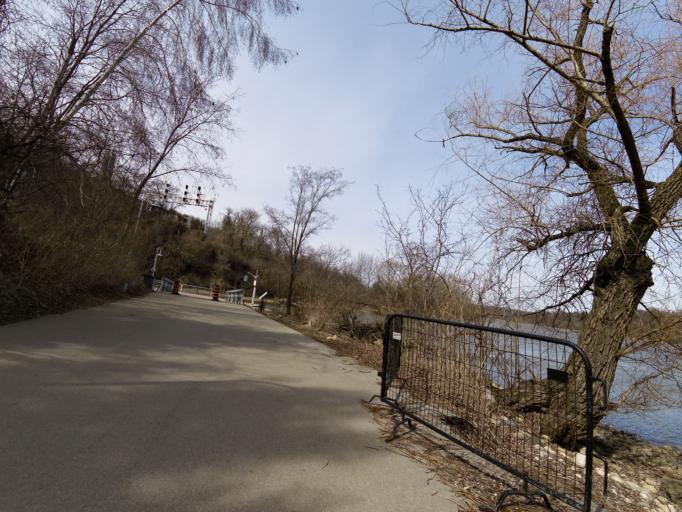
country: CA
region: Ontario
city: Hamilton
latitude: 43.2793
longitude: -79.8895
